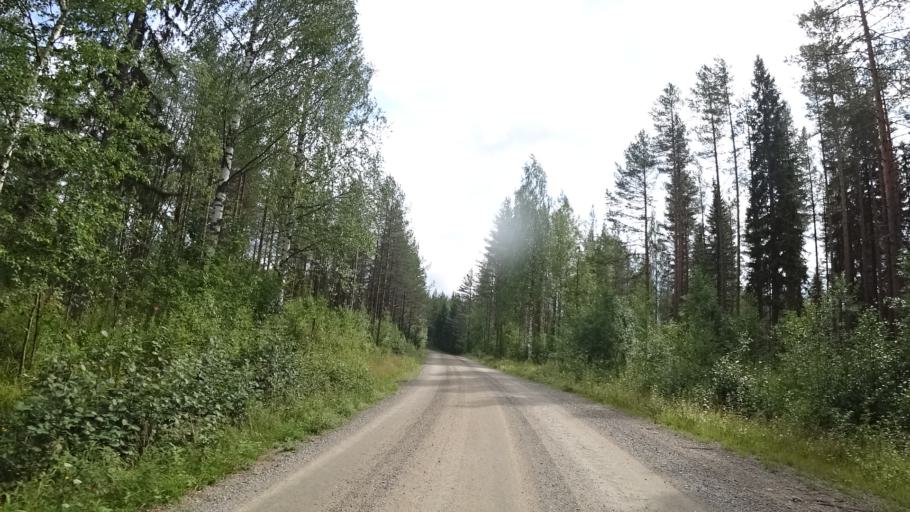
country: FI
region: North Karelia
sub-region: Joensuu
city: Ilomantsi
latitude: 62.9230
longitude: 31.3346
